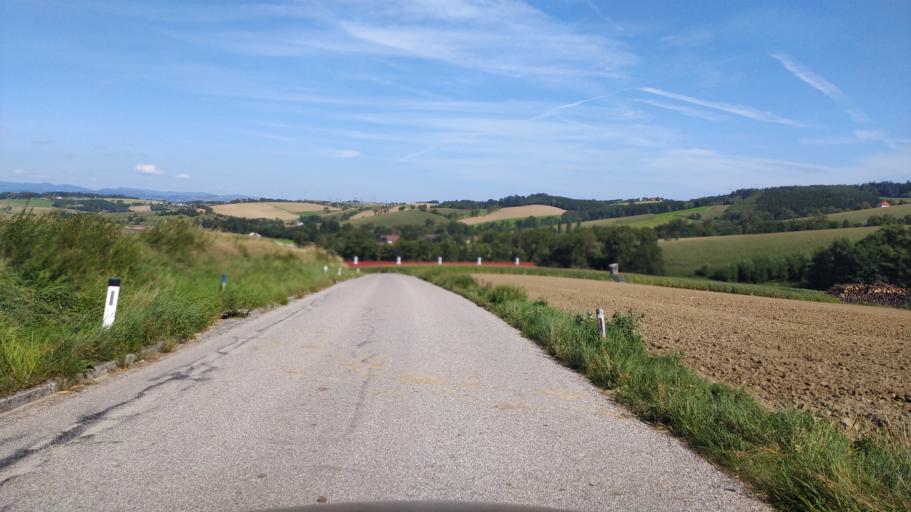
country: AT
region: Lower Austria
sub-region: Politischer Bezirk Amstetten
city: Strengberg
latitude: 48.1229
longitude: 14.6533
